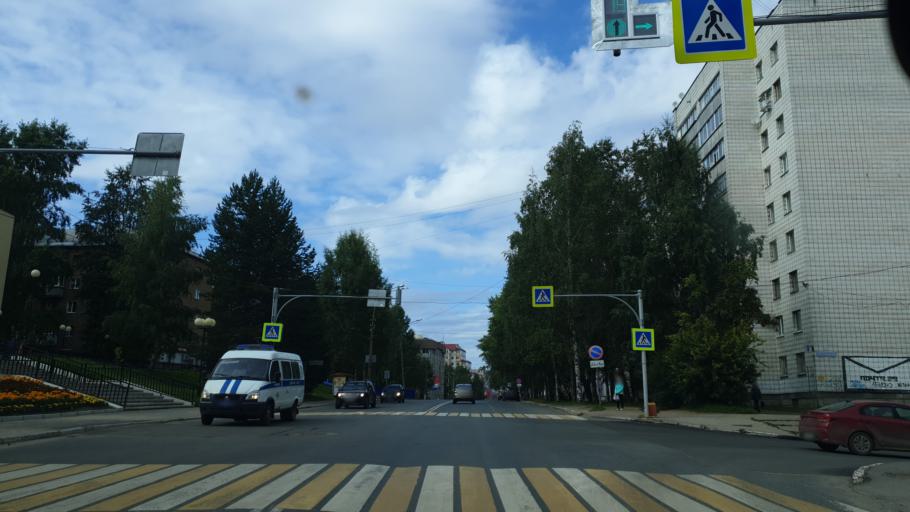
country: RU
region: Komi Republic
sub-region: Syktyvdinskiy Rayon
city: Syktyvkar
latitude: 61.6695
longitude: 50.8266
